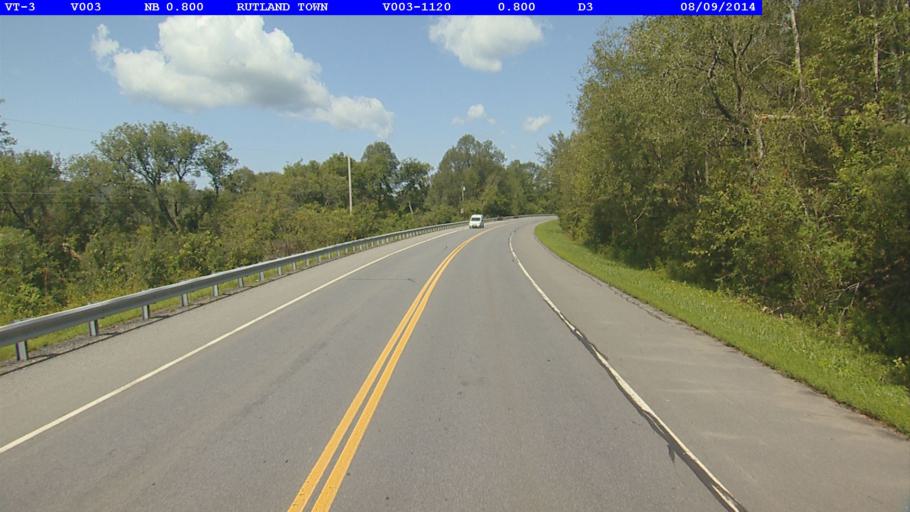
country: US
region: Vermont
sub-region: Rutland County
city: West Rutland
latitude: 43.6148
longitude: -73.0187
